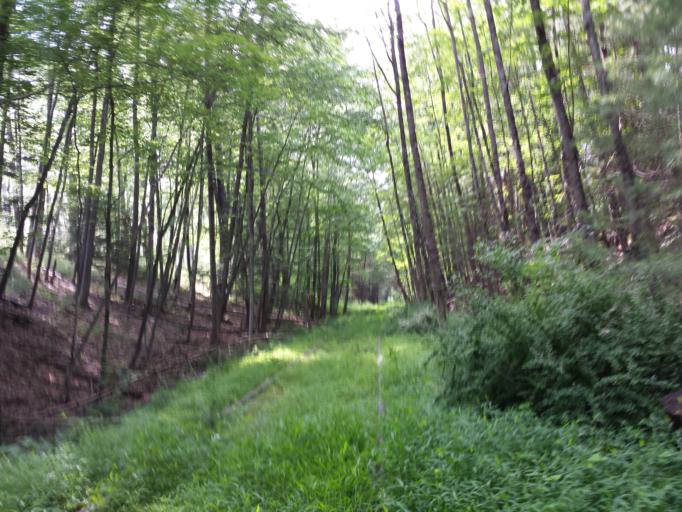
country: US
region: New York
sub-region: Ulster County
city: Shokan
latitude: 41.9683
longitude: -74.2318
